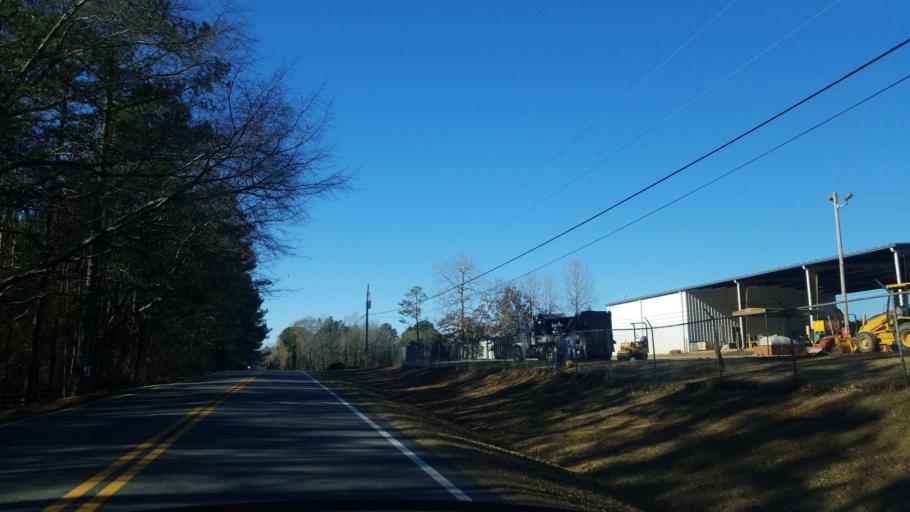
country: US
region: Georgia
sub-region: Harris County
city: Hamilton
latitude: 32.6647
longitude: -84.8699
